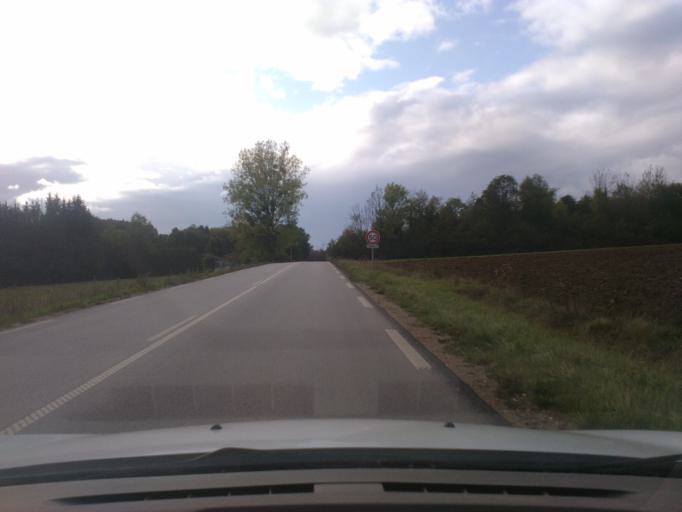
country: FR
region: Lorraine
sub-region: Departement des Vosges
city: Aydoilles
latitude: 48.2479
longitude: 6.6110
